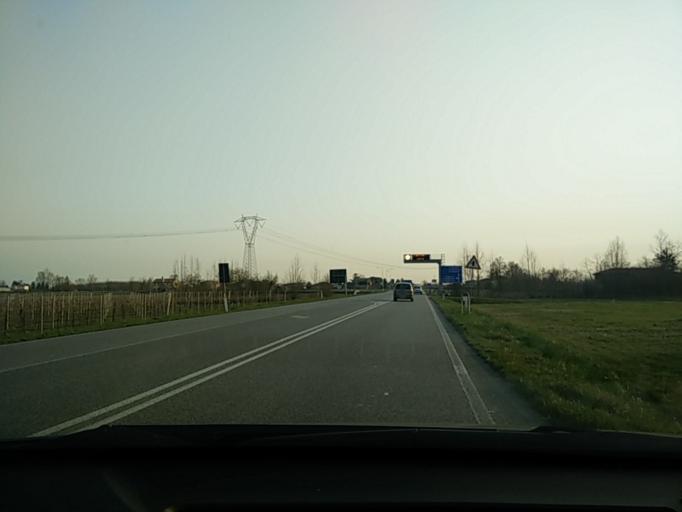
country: IT
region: Veneto
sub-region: Provincia di Treviso
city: Ponte di Piave
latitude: 45.6979
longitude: 12.4486
